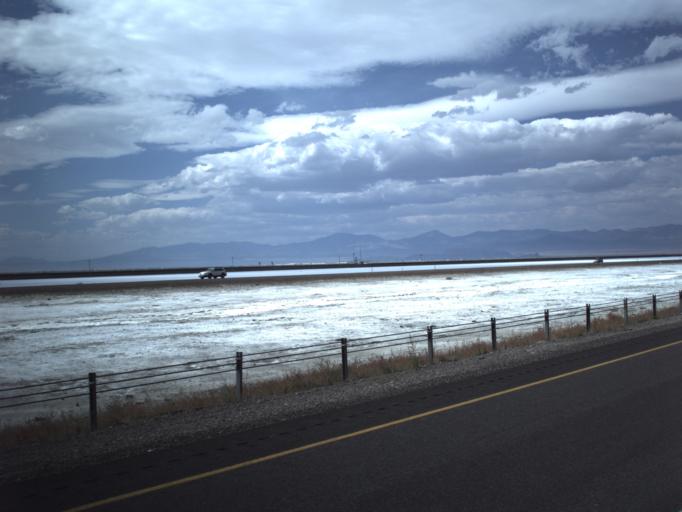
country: US
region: Utah
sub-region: Tooele County
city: Wendover
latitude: 40.7396
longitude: -113.8619
